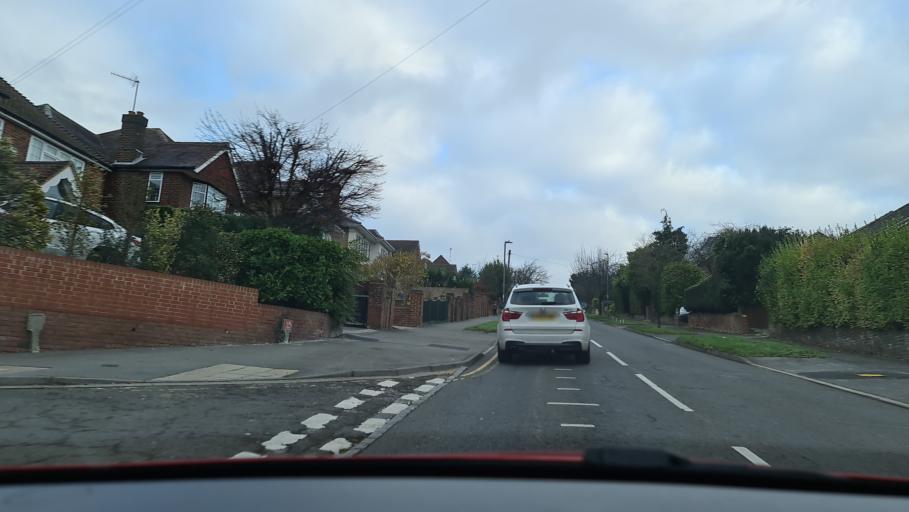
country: GB
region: England
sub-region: Buckinghamshire
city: High Wycombe
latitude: 51.6387
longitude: -0.7449
